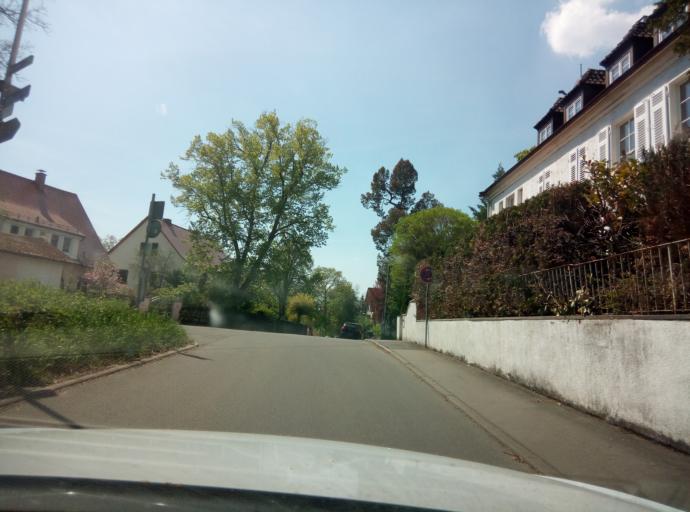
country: DE
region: Baden-Wuerttemberg
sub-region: Tuebingen Region
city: Tuebingen
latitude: 48.5221
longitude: 9.0662
